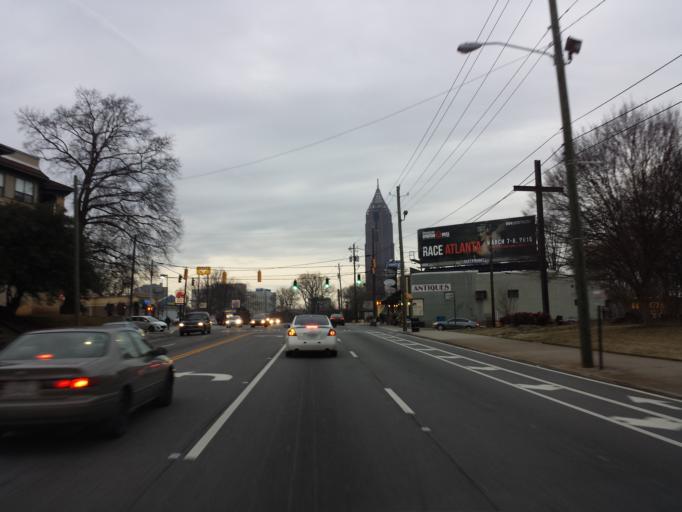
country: US
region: Georgia
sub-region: Fulton County
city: Atlanta
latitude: 33.7734
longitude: -84.3721
